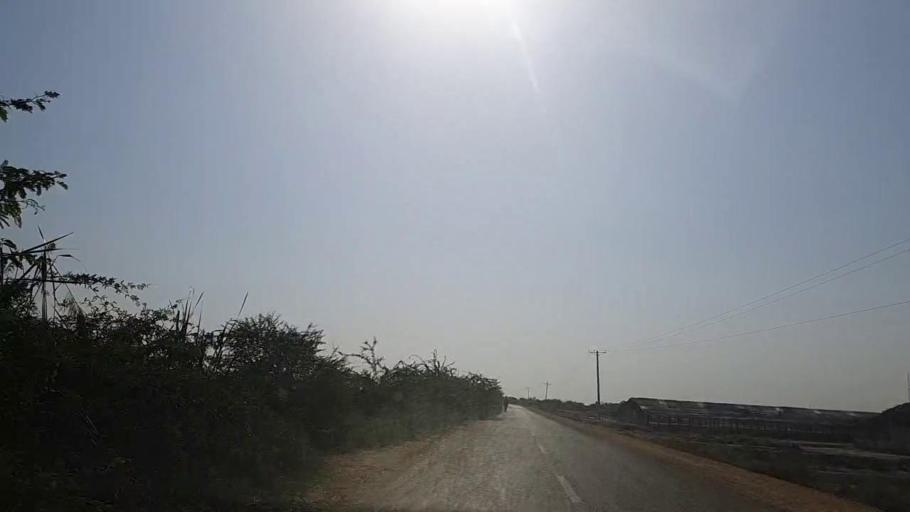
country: PK
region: Sindh
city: Jati
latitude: 24.4590
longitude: 68.2674
